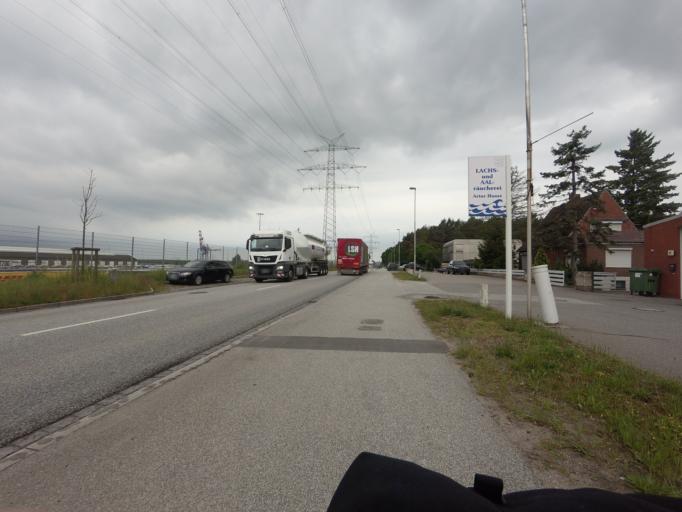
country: DE
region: Schleswig-Holstein
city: Ratekau
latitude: 53.9010
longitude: 10.7867
